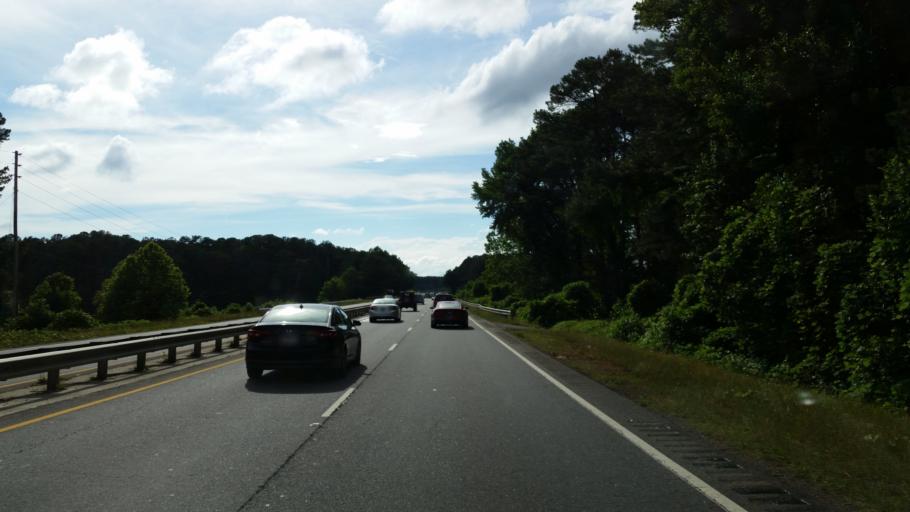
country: US
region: Georgia
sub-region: Cobb County
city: Acworth
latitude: 34.0551
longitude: -84.7072
